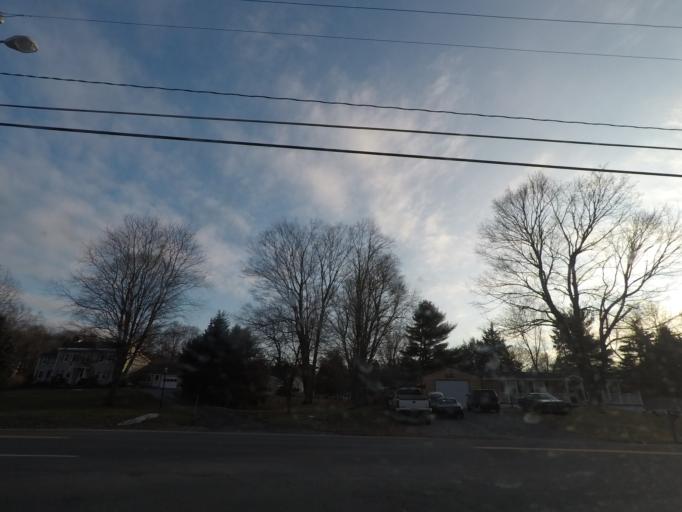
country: US
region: New York
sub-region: Rensselaer County
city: Wynantskill
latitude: 42.7174
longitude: -73.6342
